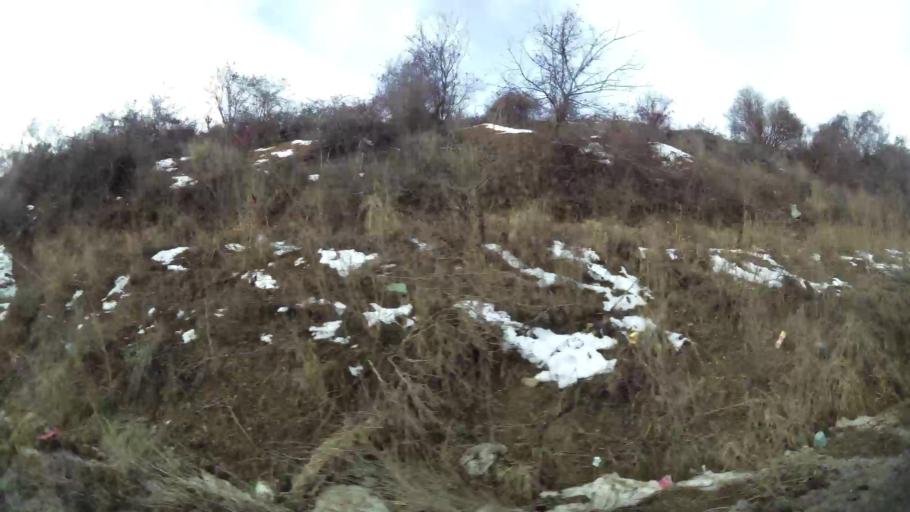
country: XK
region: Pristina
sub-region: Komuna e Prishtines
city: Pristina
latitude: 42.6874
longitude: 21.1771
